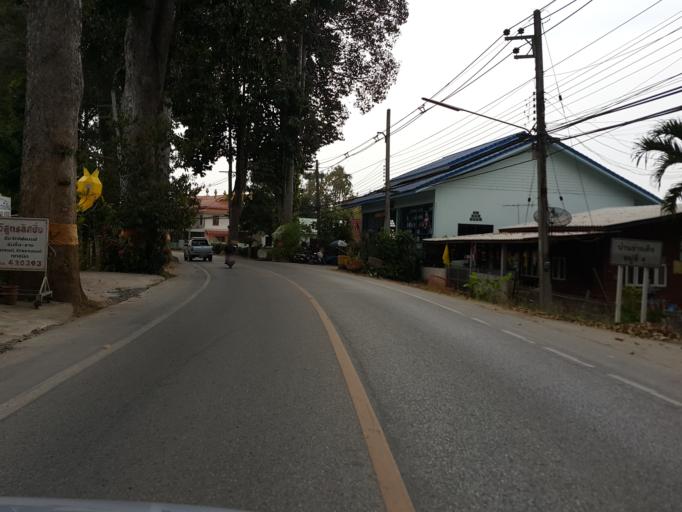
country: TH
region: Chiang Mai
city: Saraphi
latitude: 18.6902
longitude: 99.0424
